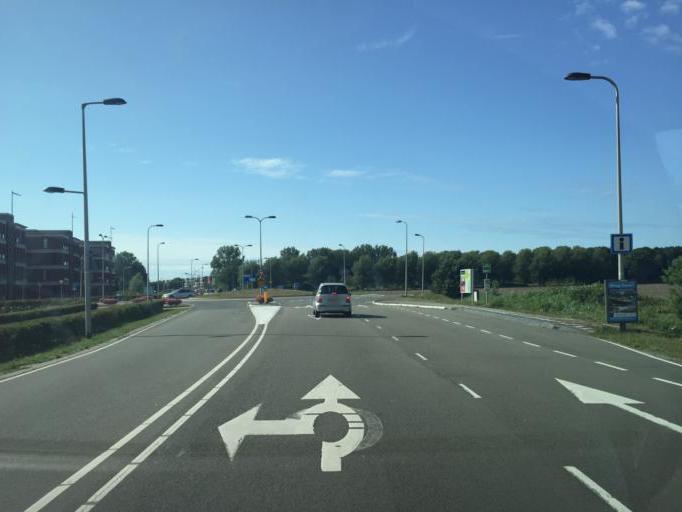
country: NL
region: South Holland
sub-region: Gemeente Noordwijk
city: Noordwijk-Binnen
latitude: 52.2359
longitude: 4.4596
